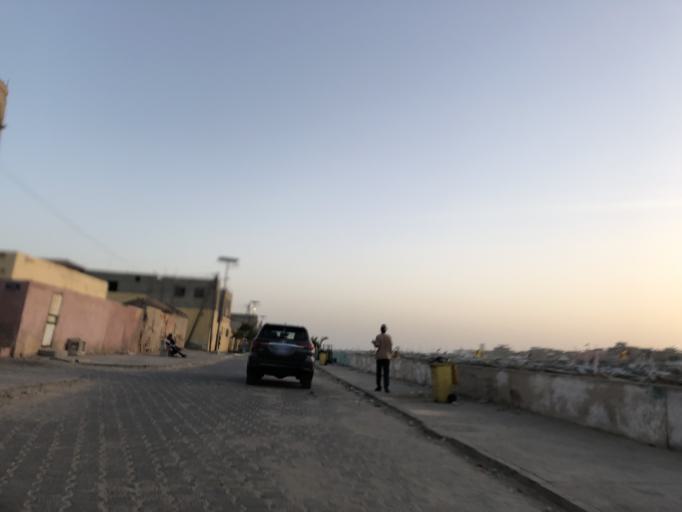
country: SN
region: Saint-Louis
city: Saint-Louis
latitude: 16.0220
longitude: -16.5065
